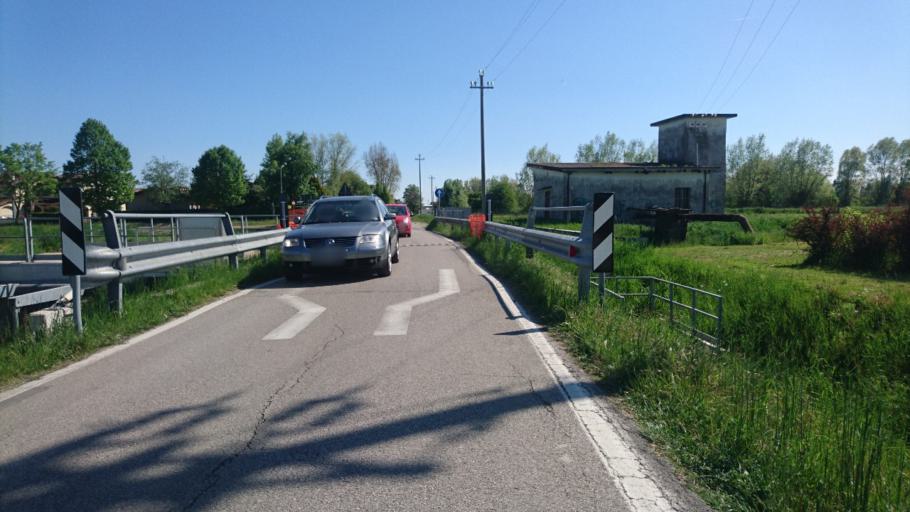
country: IT
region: Veneto
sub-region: Provincia di Venezia
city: Marcon-Gaggio-Colmello
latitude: 45.5643
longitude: 12.2912
